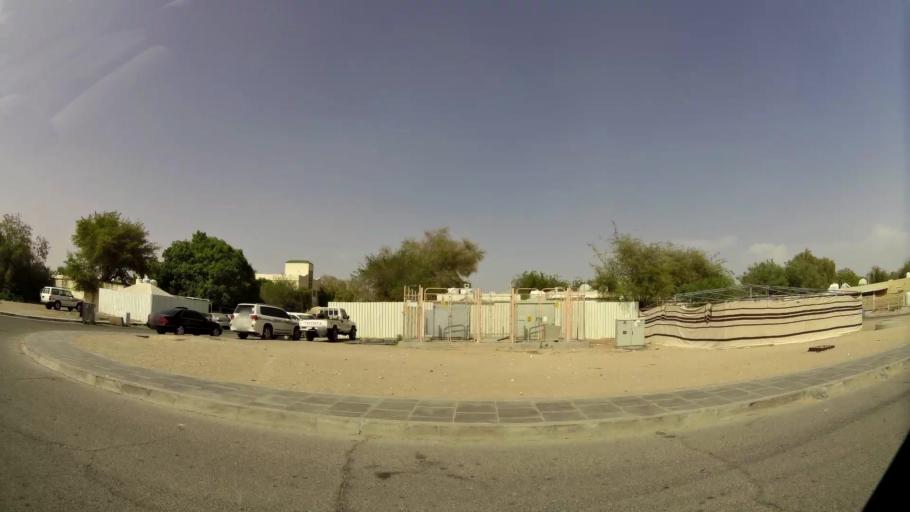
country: AE
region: Abu Dhabi
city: Al Ain
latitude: 24.2316
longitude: 55.6945
